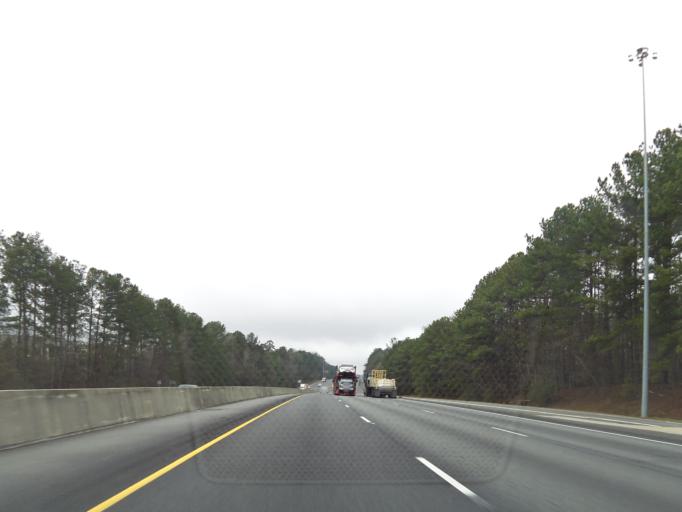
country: US
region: Georgia
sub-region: Bibb County
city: West Point
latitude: 32.8832
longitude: -83.7723
